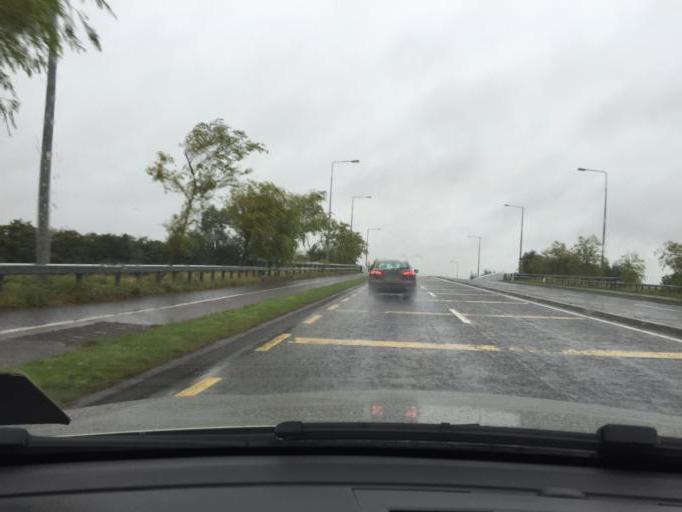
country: IE
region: Leinster
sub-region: Kildare
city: Leixlip
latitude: 53.3692
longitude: -6.5214
